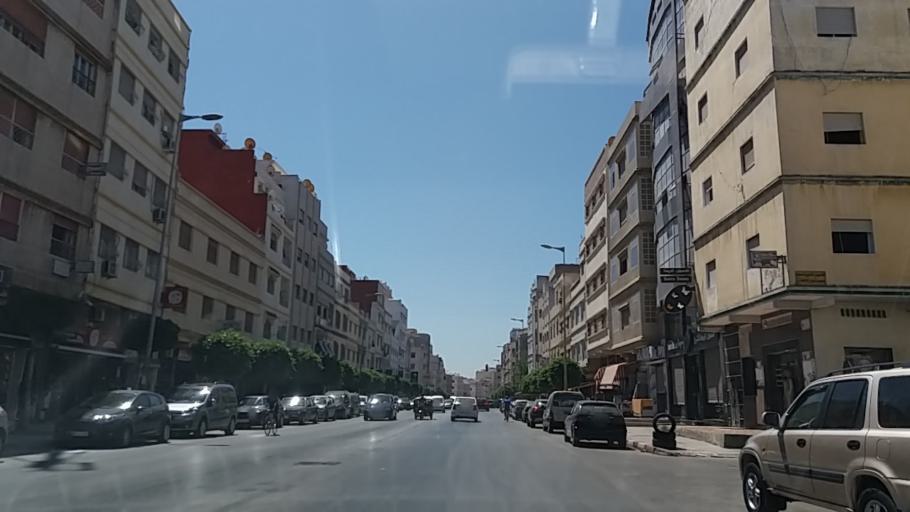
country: MA
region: Tanger-Tetouan
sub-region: Tanger-Assilah
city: Tangier
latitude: 35.7612
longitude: -5.8028
